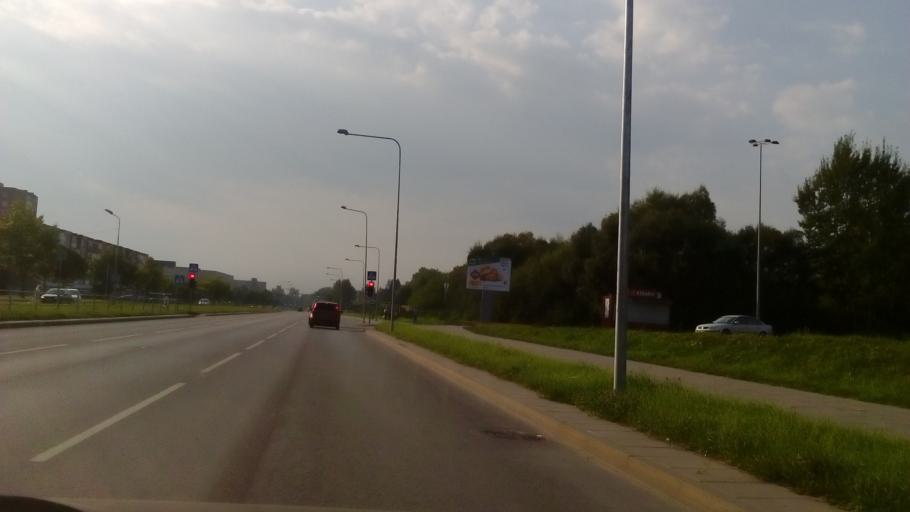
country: LT
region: Alytaus apskritis
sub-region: Alytus
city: Alytus
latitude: 54.4074
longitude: 24.0178
